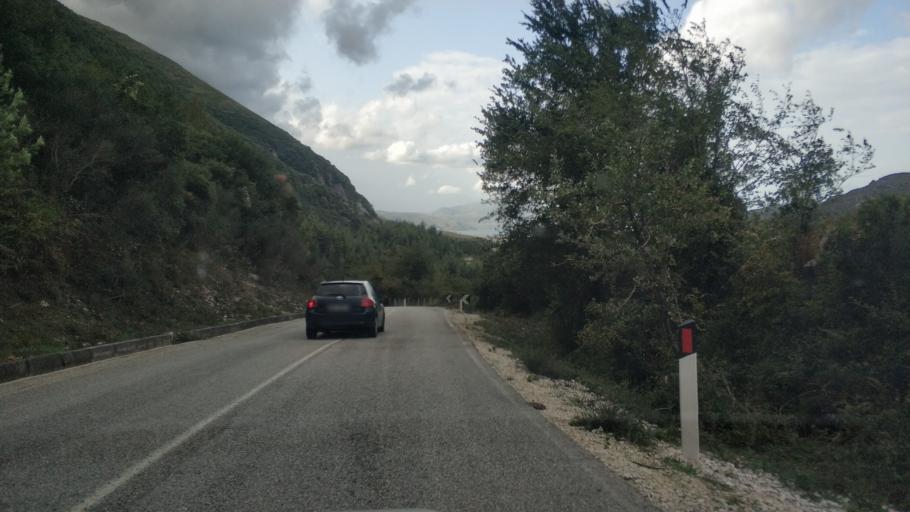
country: AL
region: Vlore
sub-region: Rrethi i Vlores
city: Orikum
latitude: 40.2548
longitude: 19.5326
